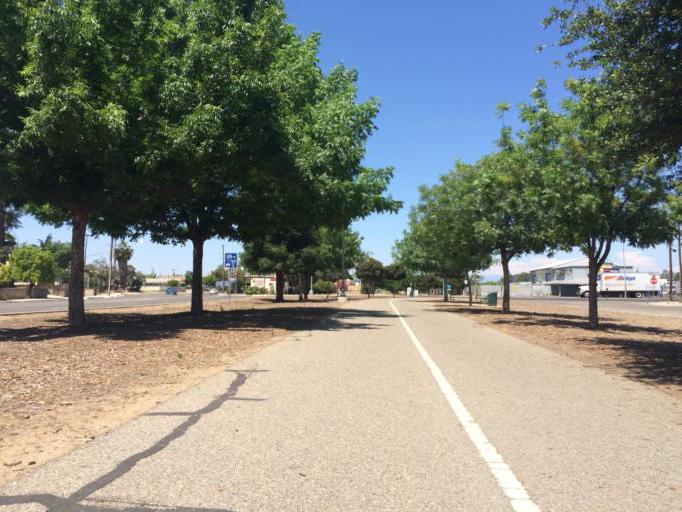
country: US
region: California
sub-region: Fresno County
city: Clovis
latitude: 36.8168
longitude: -119.7001
